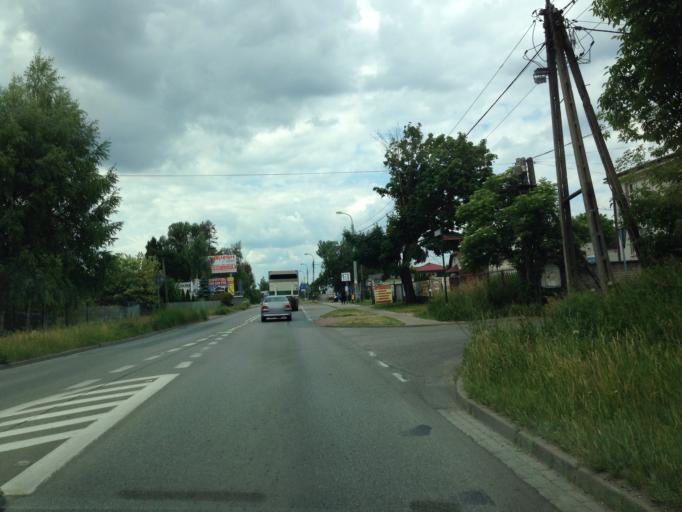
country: PL
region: Masovian Voivodeship
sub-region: Powiat warszawski zachodni
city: Babice
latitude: 52.2423
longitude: 20.8744
